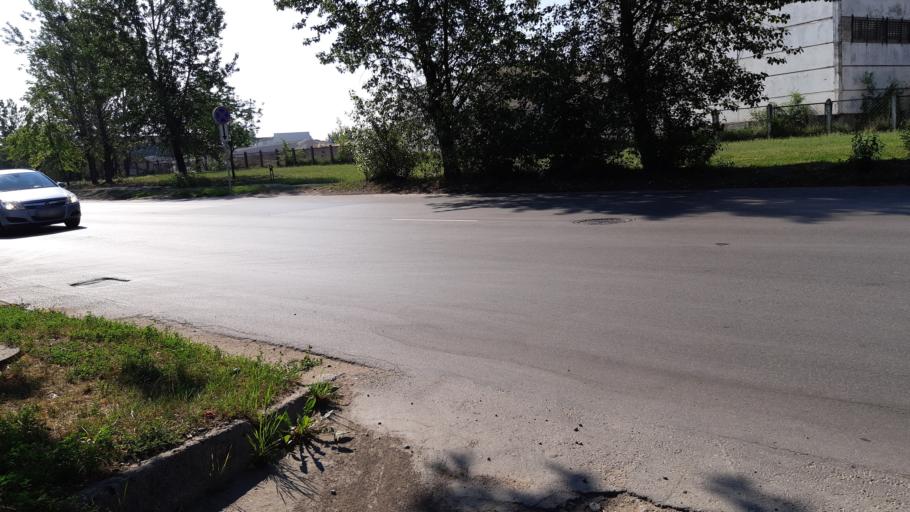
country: LT
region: Kauno apskritis
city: Dainava (Kaunas)
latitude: 54.9137
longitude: 23.9876
